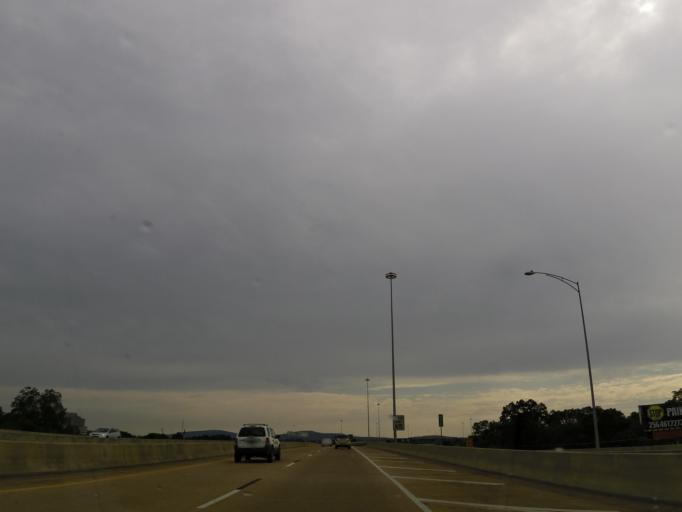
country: US
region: Alabama
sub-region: Madison County
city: Huntsville
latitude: 34.7413
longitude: -86.5837
